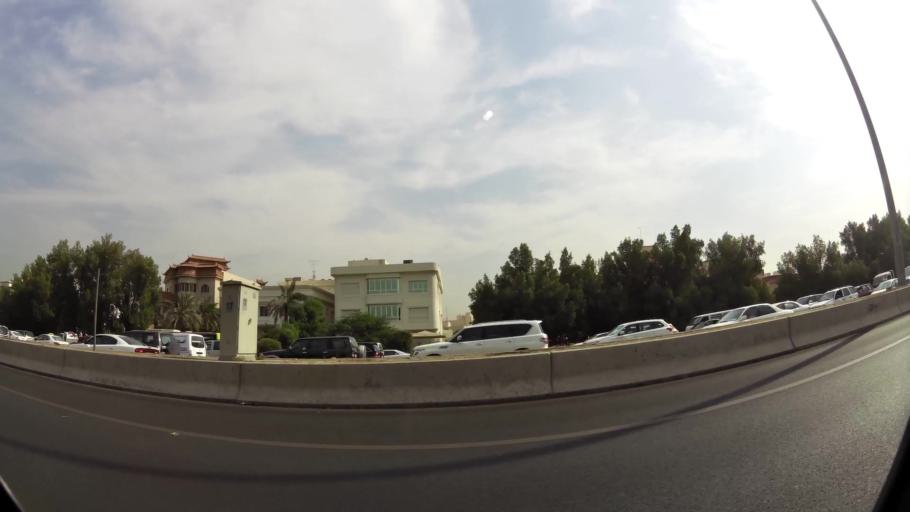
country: KW
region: Al Asimah
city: Ash Shamiyah
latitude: 29.3122
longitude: 47.9765
